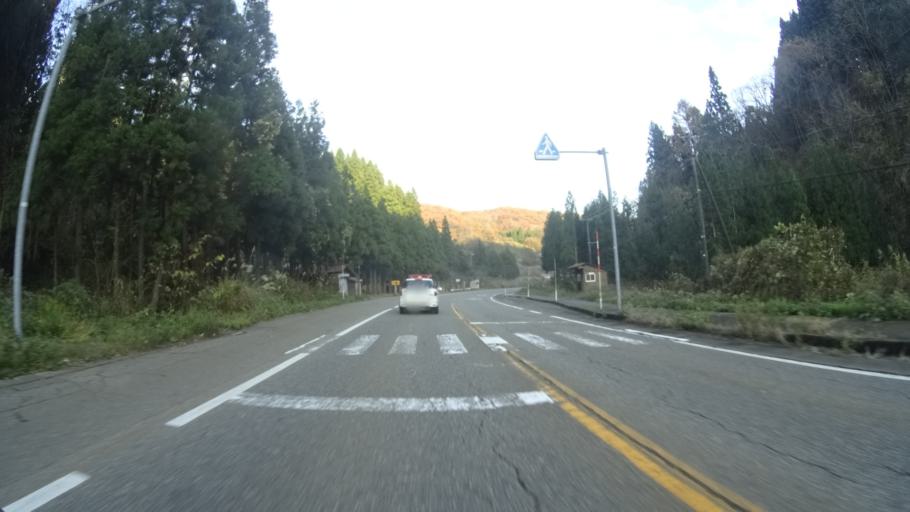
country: JP
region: Niigata
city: Kashiwazaki
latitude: 37.4129
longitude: 138.6803
